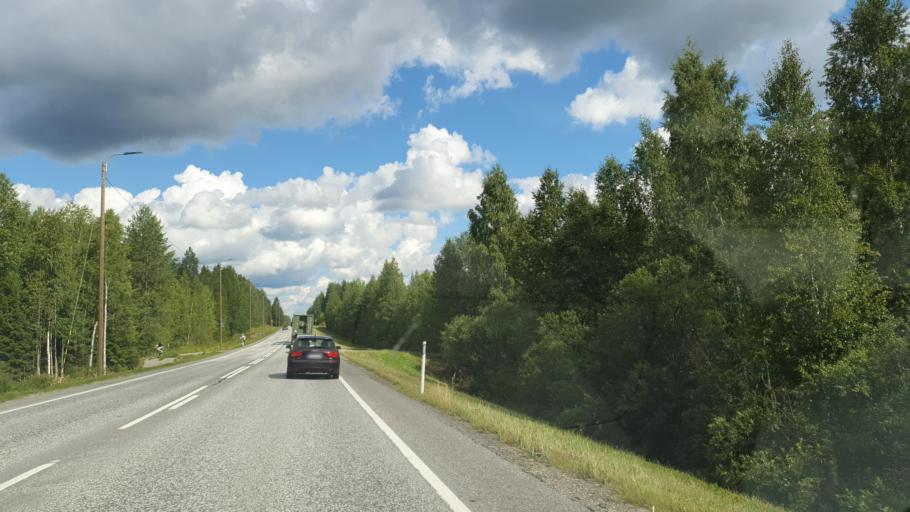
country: FI
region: Kainuu
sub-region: Kajaani
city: Kajaani
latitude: 64.1969
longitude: 27.6295
